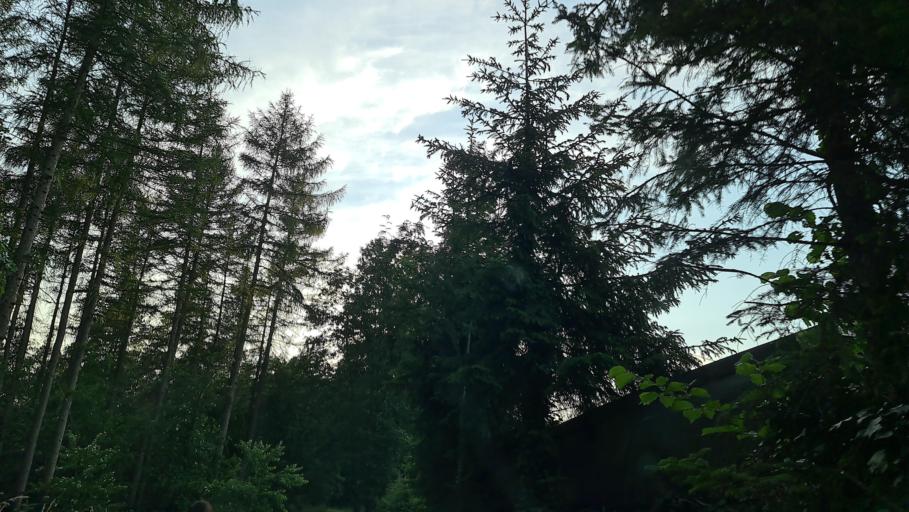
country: DE
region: Saxony
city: Hohndorf
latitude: 50.7319
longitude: 12.6797
